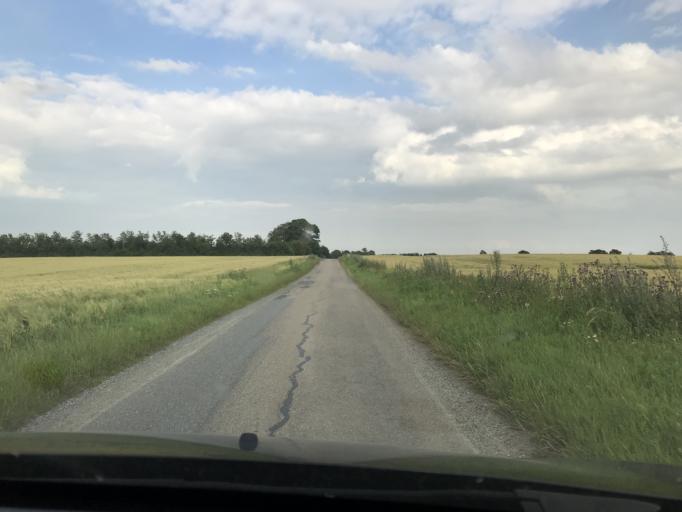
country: DK
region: South Denmark
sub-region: Vejle Kommune
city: Jelling
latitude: 55.8050
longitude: 9.4136
